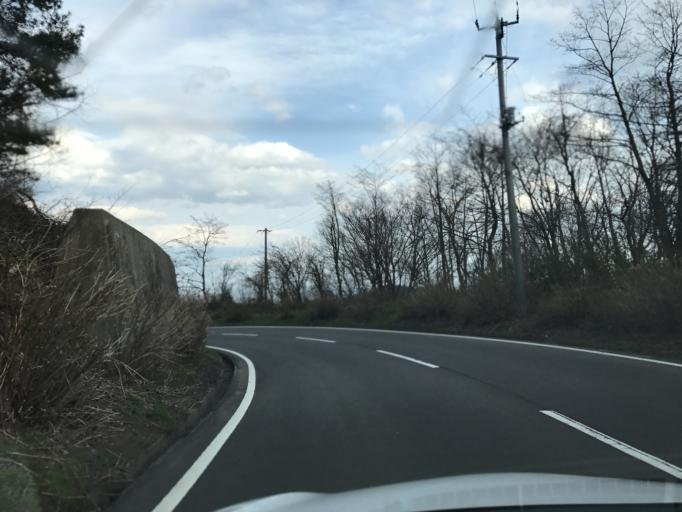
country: JP
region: Miyagi
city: Shiroishi
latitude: 38.0206
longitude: 140.5530
